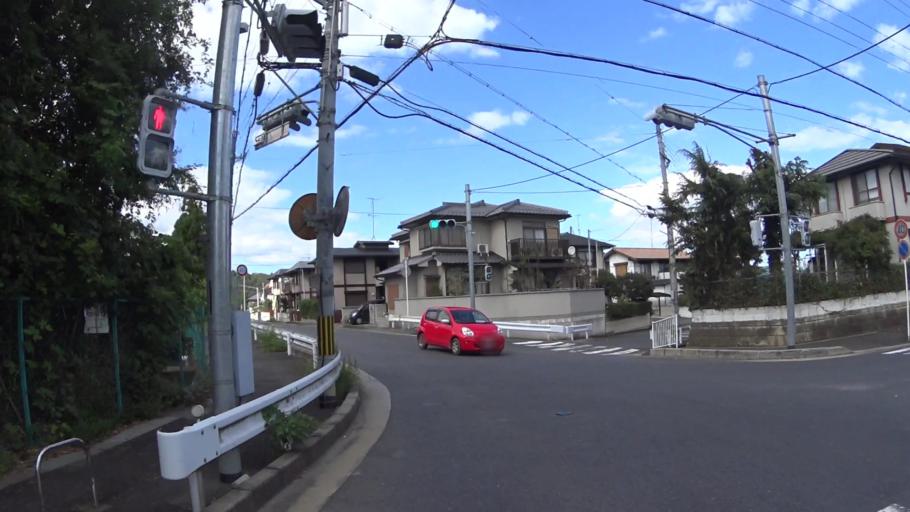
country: JP
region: Shiga Prefecture
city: Otsu-shi
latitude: 34.9416
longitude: 135.8980
